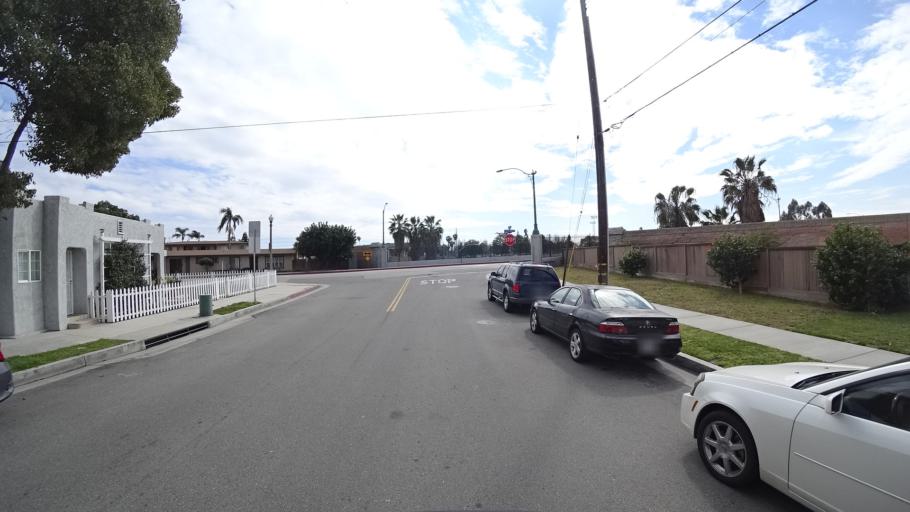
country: US
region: California
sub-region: Orange County
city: Anaheim
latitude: 33.8302
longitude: -117.9285
